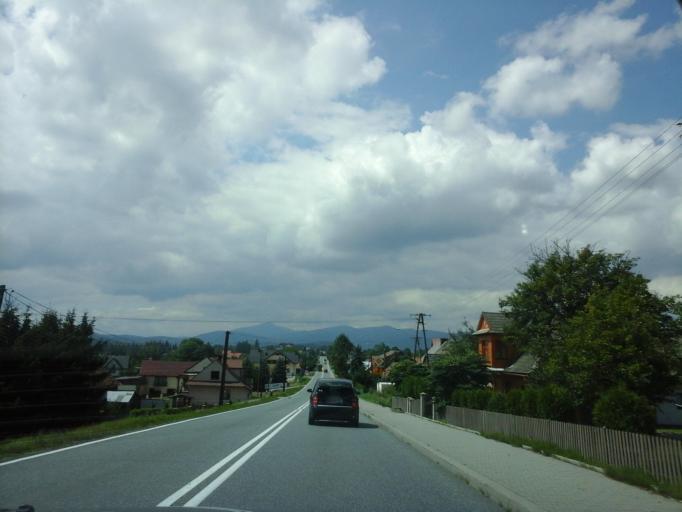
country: PL
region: Lesser Poland Voivodeship
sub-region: Powiat suski
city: Naprawa
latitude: 49.6465
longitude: 19.8812
